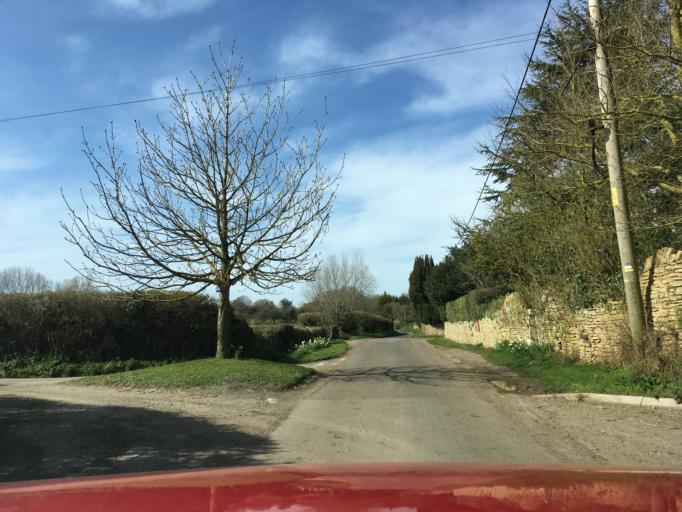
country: GB
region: England
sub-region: Wiltshire
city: Chippenham
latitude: 51.4742
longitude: -2.1517
